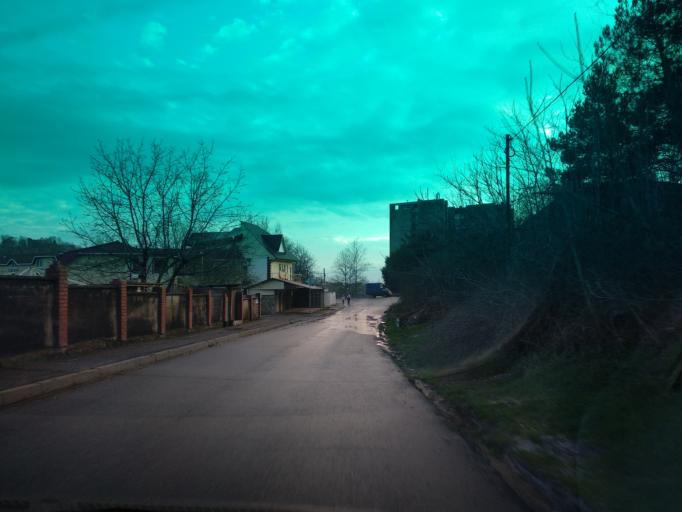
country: RU
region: Krasnodarskiy
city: Novomikhaylovskiy
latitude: 44.2613
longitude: 38.8223
